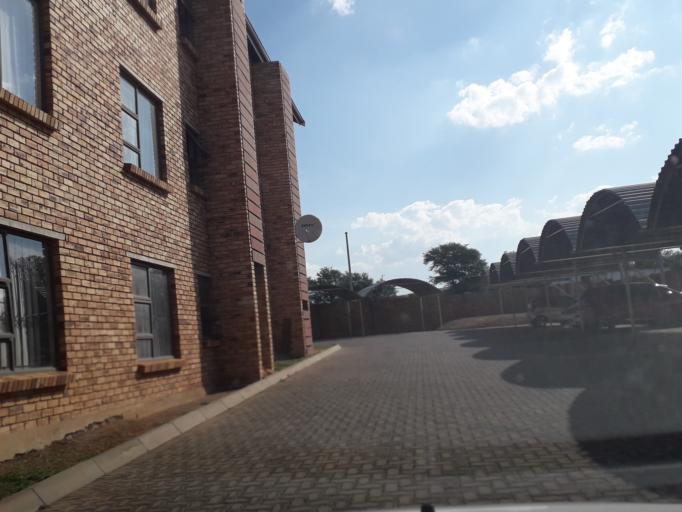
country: ZA
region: Gauteng
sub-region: West Rand District Municipality
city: Muldersdriseloop
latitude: -26.0666
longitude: 27.9072
